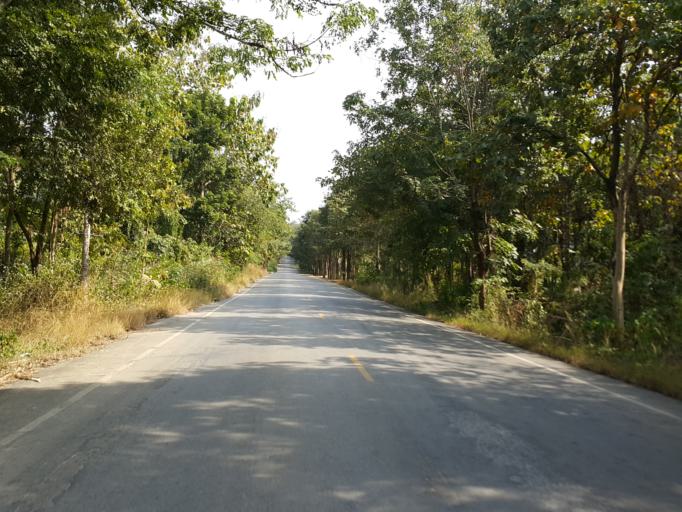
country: TH
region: Sukhothai
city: Thung Saliam
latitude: 17.3439
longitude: 99.4493
